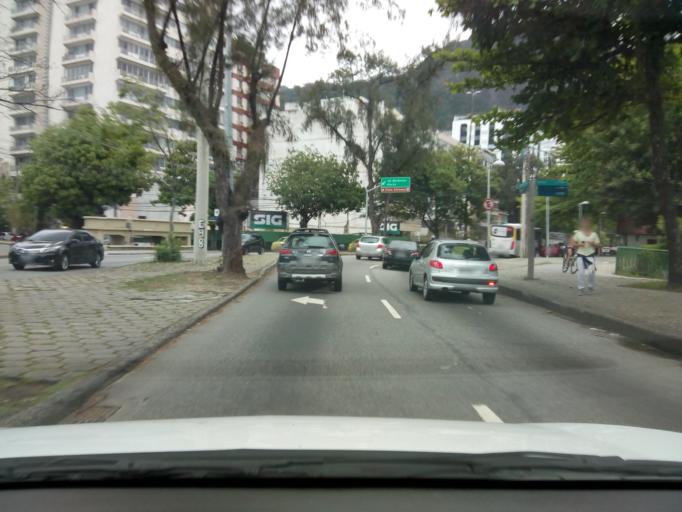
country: BR
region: Rio de Janeiro
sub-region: Rio De Janeiro
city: Rio de Janeiro
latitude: -22.9680
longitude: -43.2174
